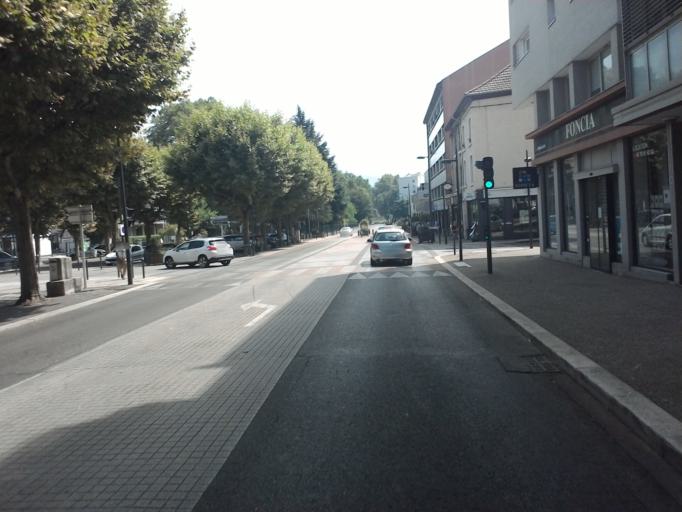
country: FR
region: Rhone-Alpes
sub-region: Departement de l'Isere
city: Voiron
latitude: 45.3638
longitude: 5.5908
